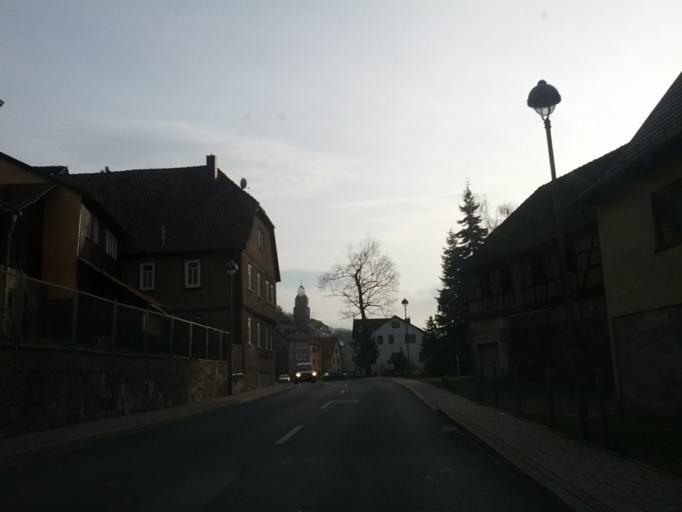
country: DE
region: Thuringia
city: Wasungen
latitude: 50.6669
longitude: 10.3645
